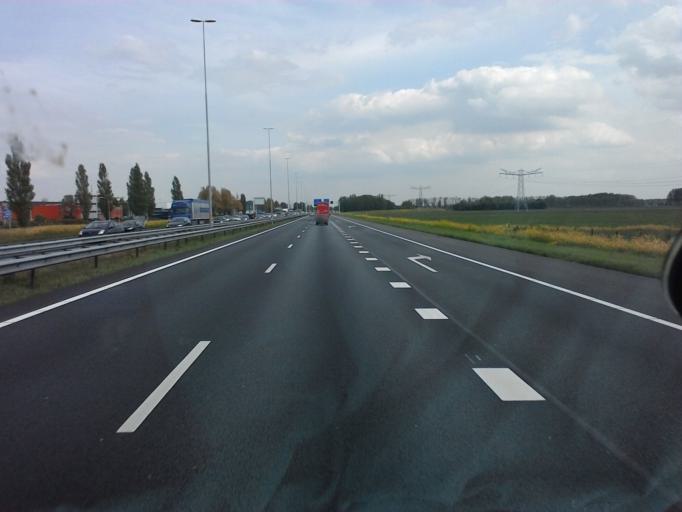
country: NL
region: Gelderland
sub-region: Gemeente Beuningen
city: Beuningen
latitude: 51.8535
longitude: 5.7334
